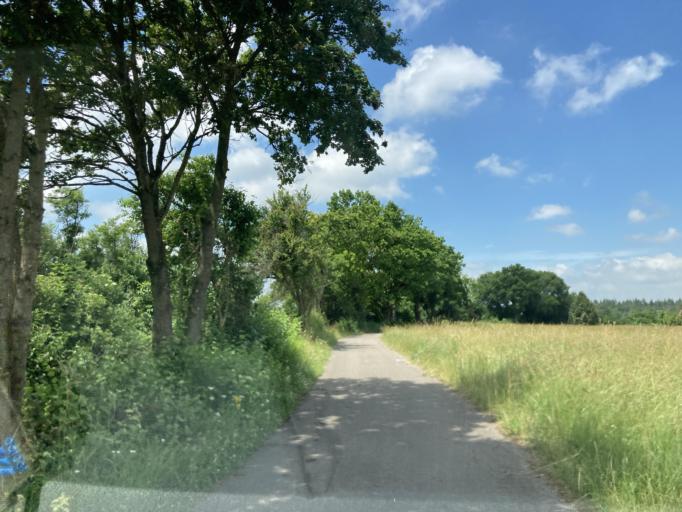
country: DE
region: Baden-Wuerttemberg
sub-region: Karlsruhe Region
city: Graben-Neudorf
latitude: 49.1844
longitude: 8.5114
